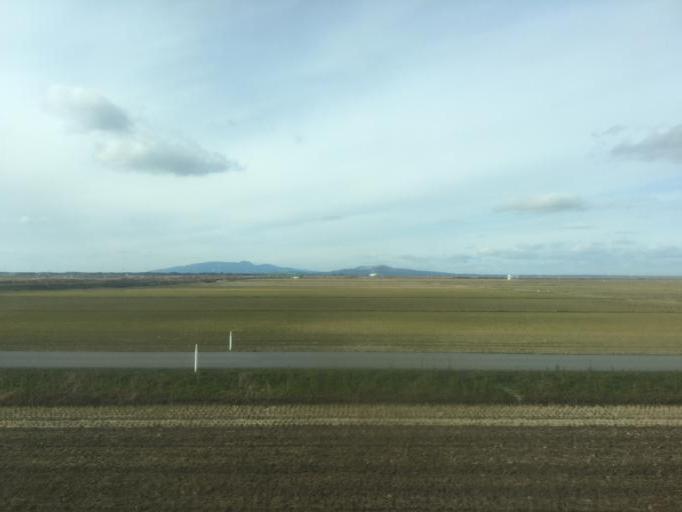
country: JP
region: Akita
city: Tenno
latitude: 39.8797
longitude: 140.0661
